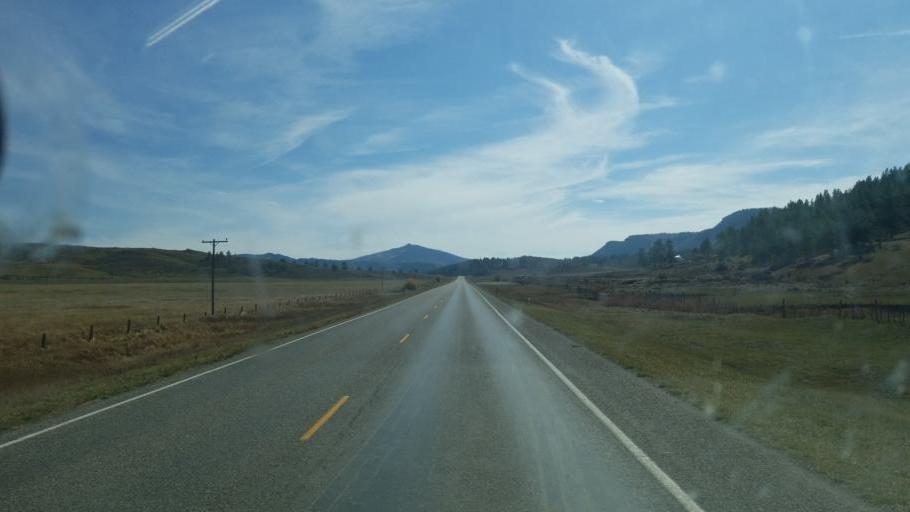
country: US
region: New Mexico
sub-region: Rio Arriba County
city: Dulce
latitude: 37.0313
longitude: -106.8290
